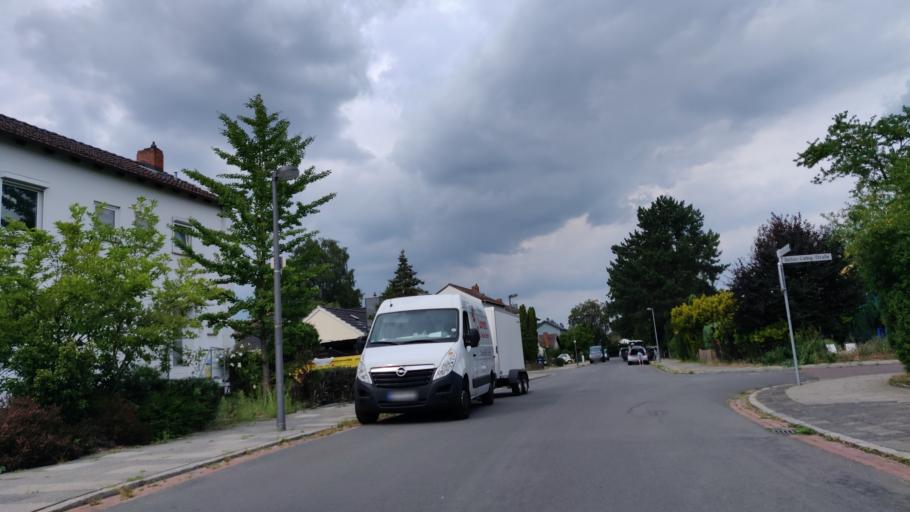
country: DE
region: Lower Saxony
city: Lilienthal
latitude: 53.1028
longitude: 8.8849
